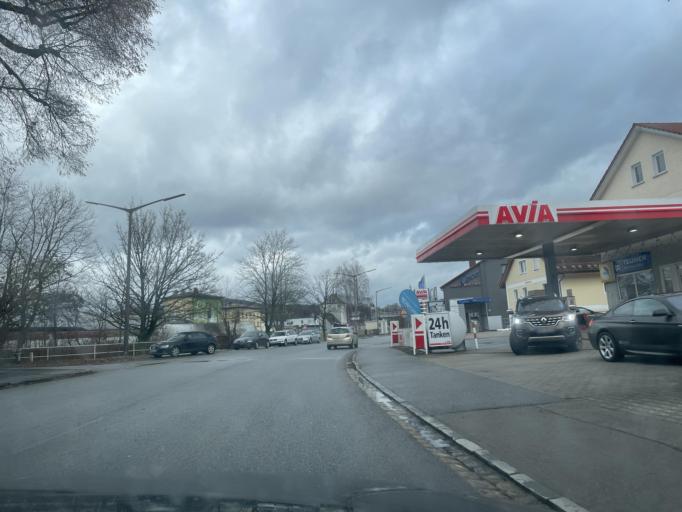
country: DE
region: Bavaria
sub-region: Upper Palatinate
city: Furth im Wald
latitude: 49.3090
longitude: 12.8357
